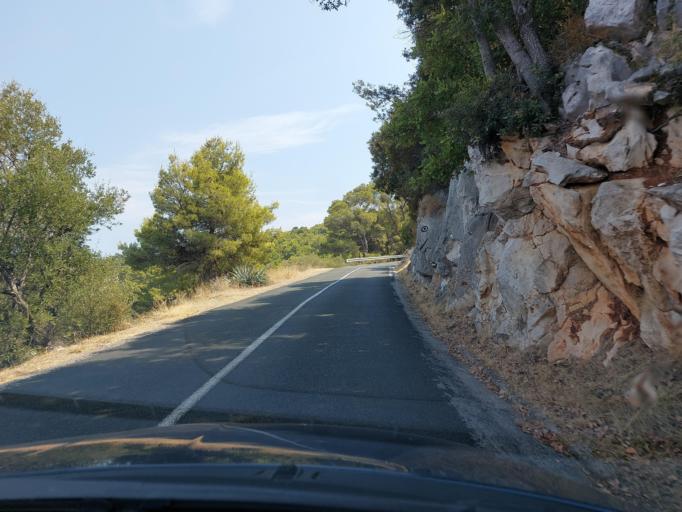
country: HR
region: Dubrovacko-Neretvanska
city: Smokvica
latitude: 42.7689
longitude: 16.8853
